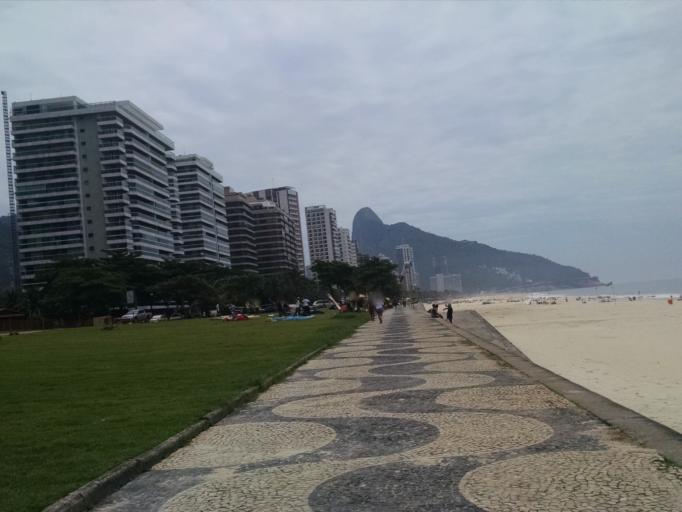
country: BR
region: Rio de Janeiro
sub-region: Rio De Janeiro
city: Rio de Janeiro
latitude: -23.0014
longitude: -43.2738
